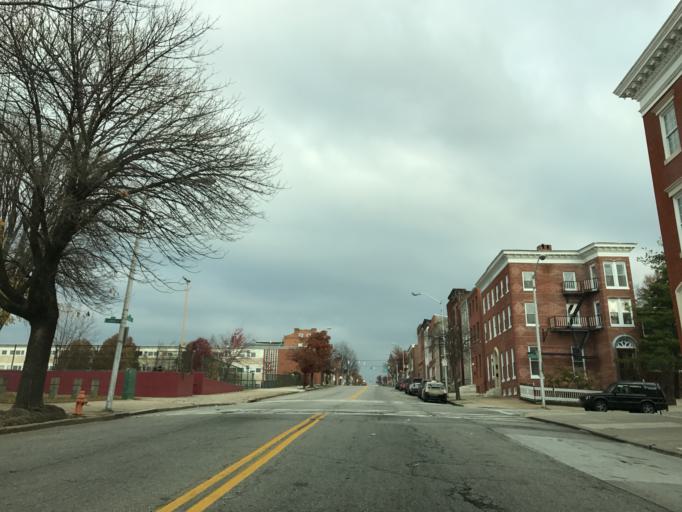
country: US
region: Maryland
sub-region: City of Baltimore
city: Baltimore
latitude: 39.3028
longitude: -76.5979
